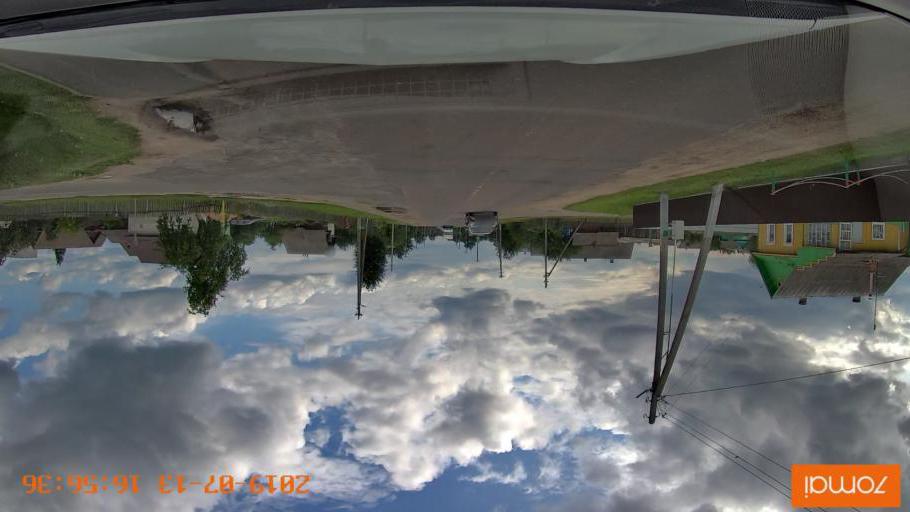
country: BY
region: Mogilev
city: Kirawsk
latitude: 53.2744
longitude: 29.4580
